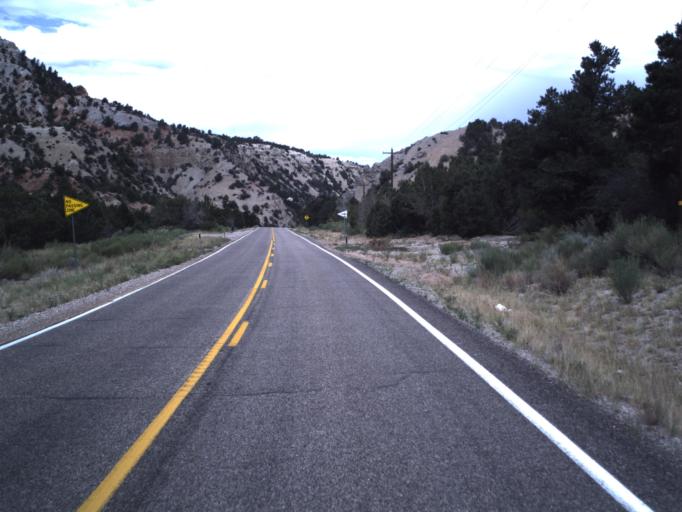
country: US
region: Utah
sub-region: Iron County
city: Cedar City
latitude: 37.6656
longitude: -113.0026
